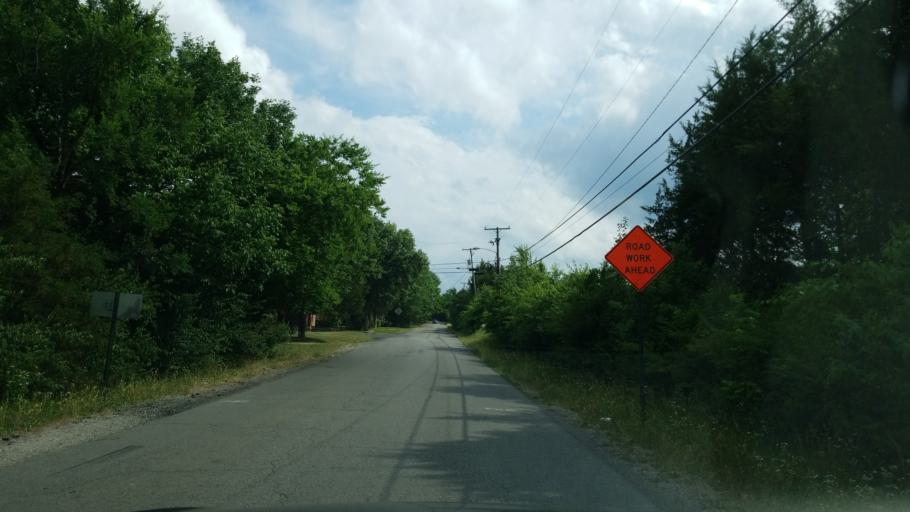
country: US
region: Tennessee
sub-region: Rutherford County
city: La Vergne
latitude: 36.0859
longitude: -86.6177
